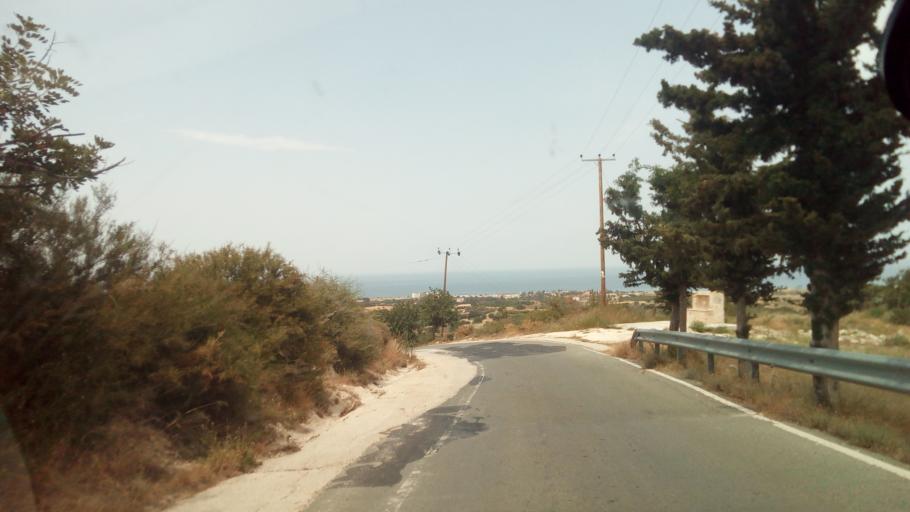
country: CY
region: Pafos
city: Polis
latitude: 35.0172
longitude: 32.3969
